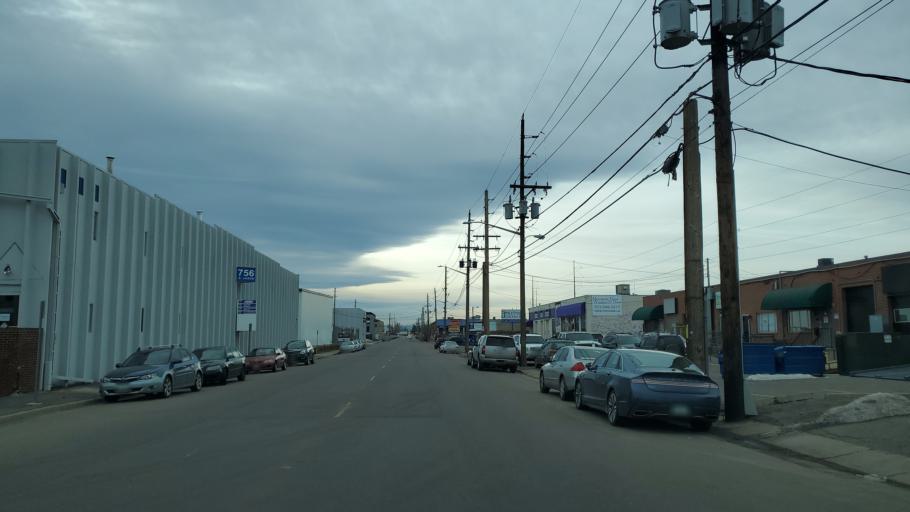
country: US
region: Colorado
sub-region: Denver County
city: Denver
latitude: 39.7028
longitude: -104.9992
